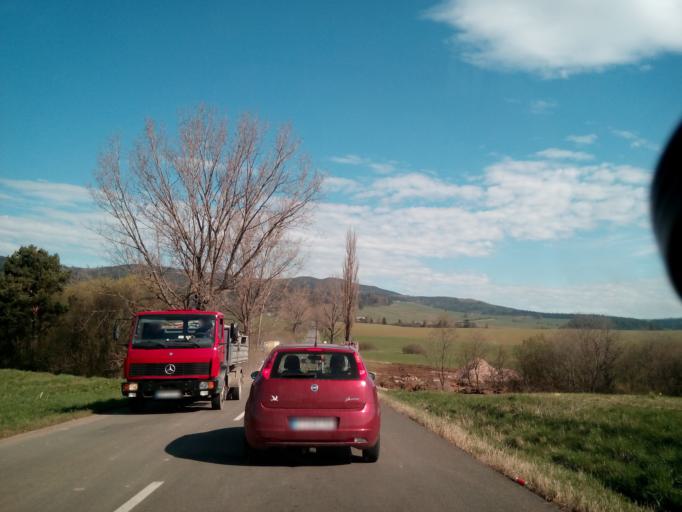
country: SK
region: Presovsky
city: Spisska Bela
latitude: 49.2476
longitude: 20.4248
